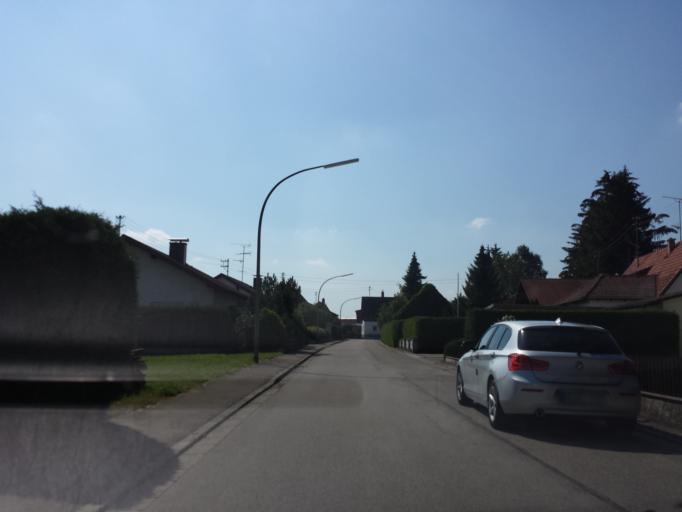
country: DE
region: Bavaria
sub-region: Swabia
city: Turkheim
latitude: 48.0659
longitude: 10.6388
